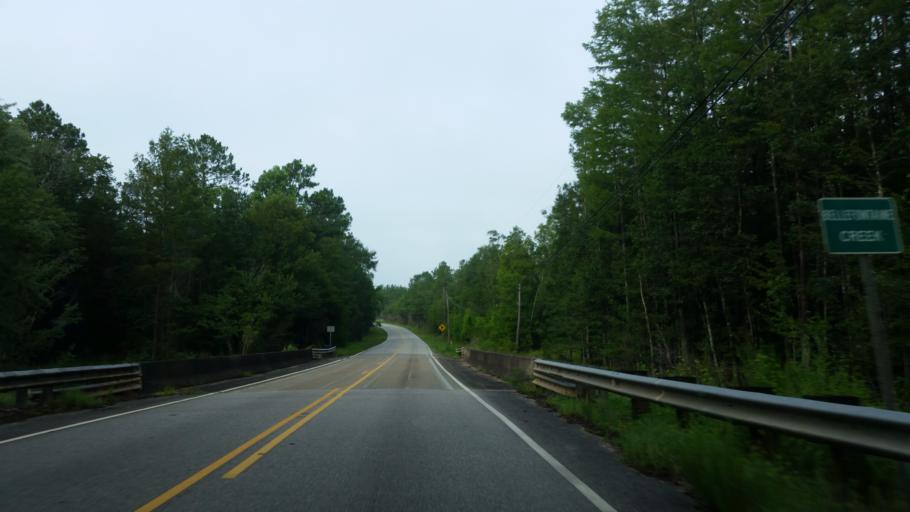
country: US
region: Florida
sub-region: Escambia County
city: Cantonment
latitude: 30.6868
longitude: -87.5277
